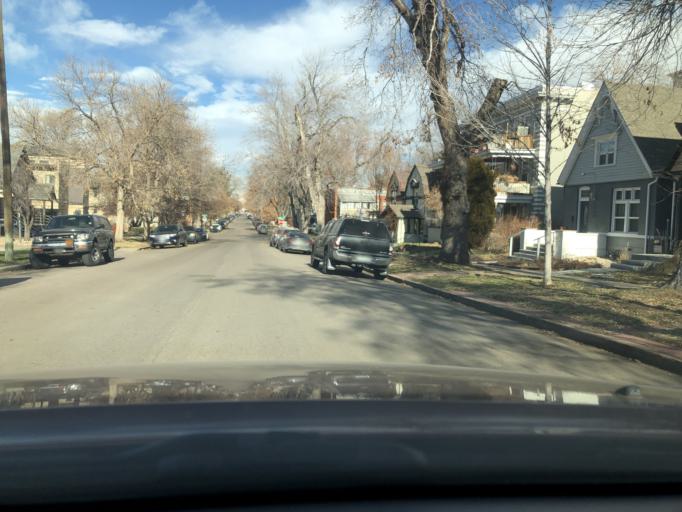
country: US
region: Colorado
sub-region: Denver County
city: Denver
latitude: 39.7407
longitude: -104.9672
